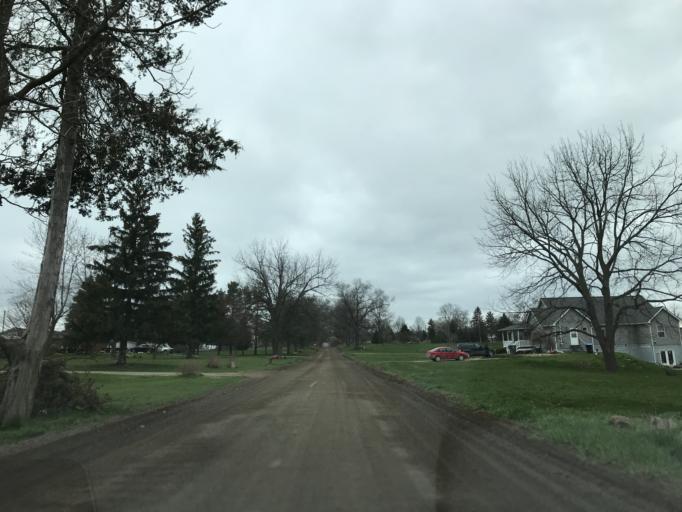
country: US
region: Michigan
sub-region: Oakland County
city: South Lyon
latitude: 42.4783
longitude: -83.6679
